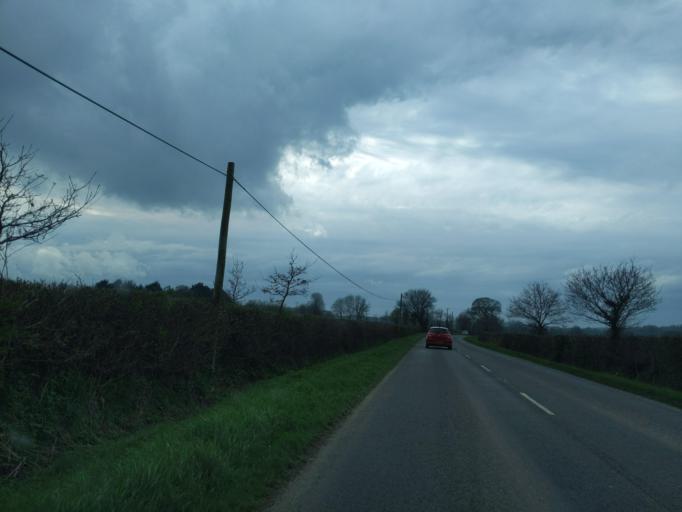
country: GB
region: England
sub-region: Devon
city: Winkleigh
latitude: 50.8490
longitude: -3.9224
